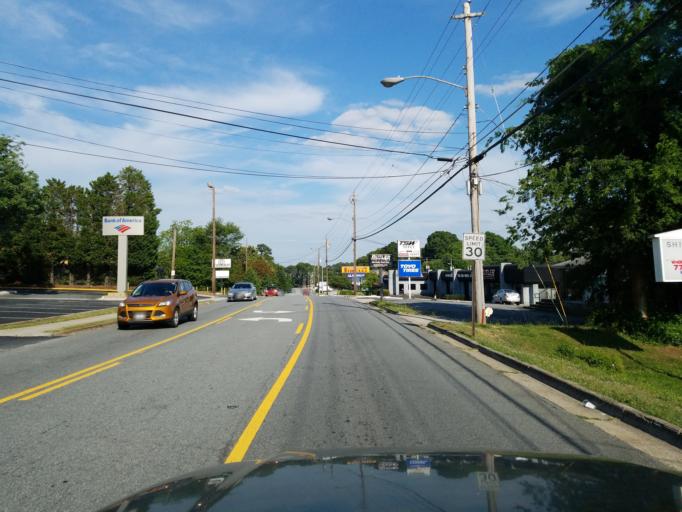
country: US
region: Georgia
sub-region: Cobb County
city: Marietta
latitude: 33.9498
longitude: -84.5110
